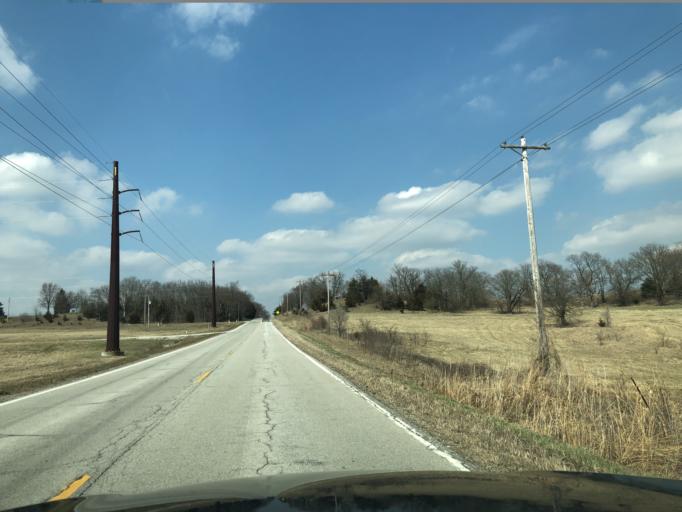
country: US
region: Missouri
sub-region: Platte County
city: Platte City
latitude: 39.4415
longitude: -94.8073
